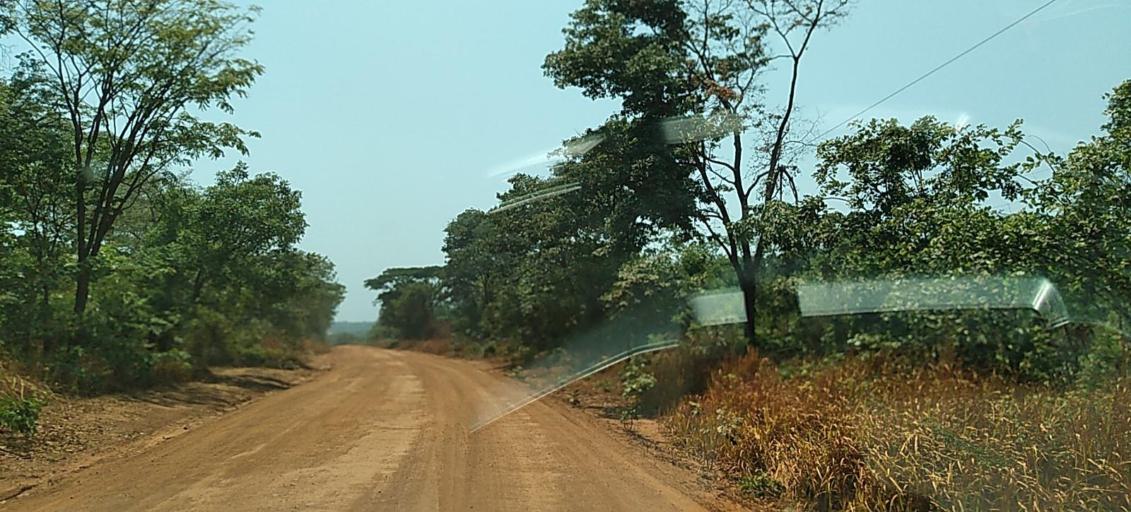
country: ZM
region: North-Western
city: Kansanshi
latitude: -11.9906
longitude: 26.8381
